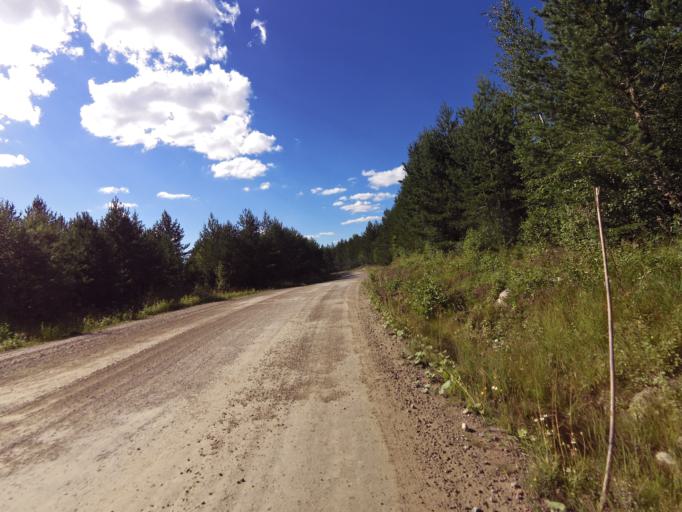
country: SE
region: Dalarna
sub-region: Faluns Kommun
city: Svardsjo
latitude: 60.6408
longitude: 15.8960
